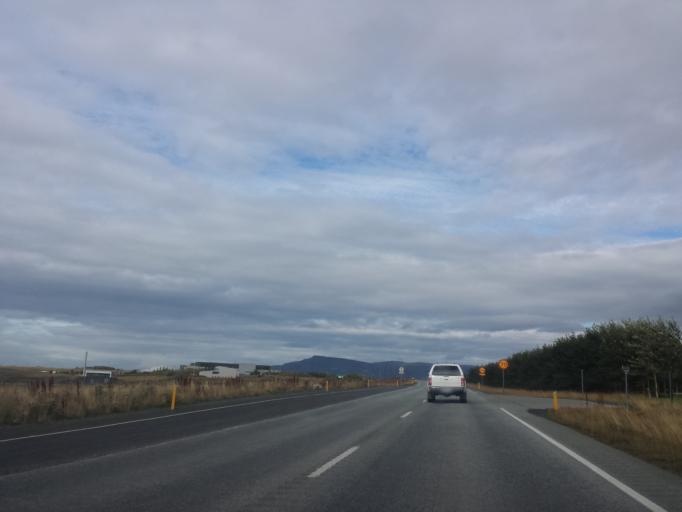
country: IS
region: Capital Region
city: Reykjavik
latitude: 64.2341
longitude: -21.8190
